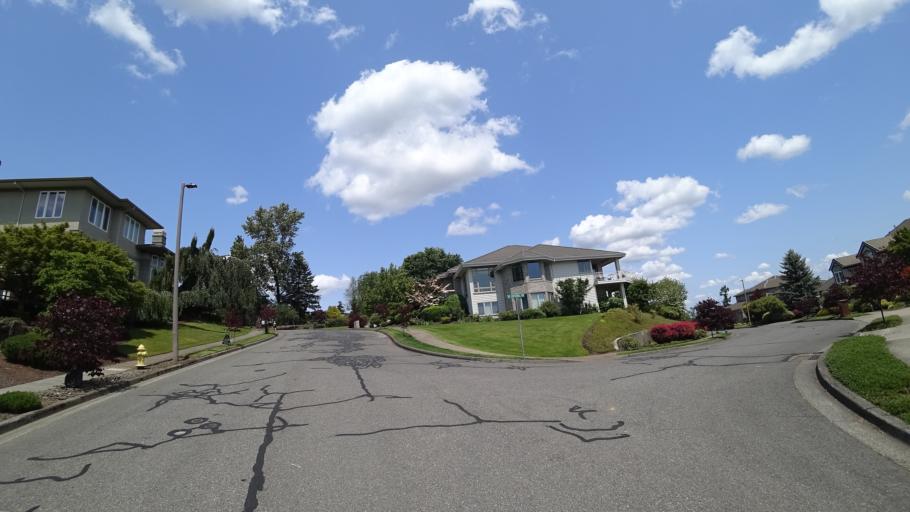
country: US
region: Oregon
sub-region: Clackamas County
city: Happy Valley
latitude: 45.4463
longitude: -122.5425
